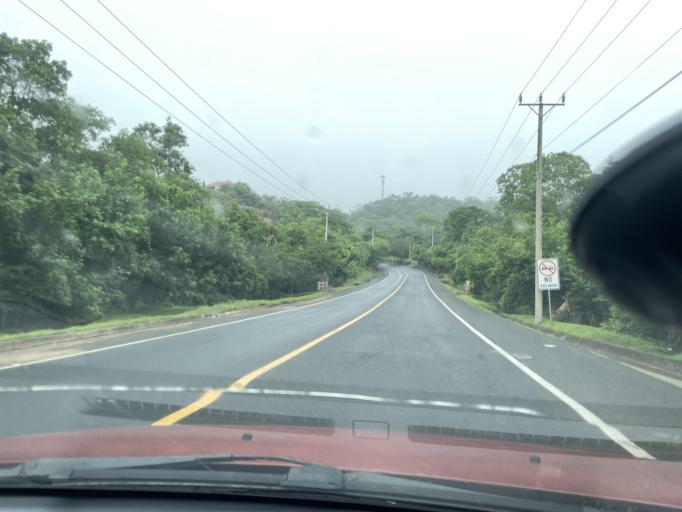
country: SV
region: San Miguel
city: San Miguel
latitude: 13.5272
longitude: -88.1420
